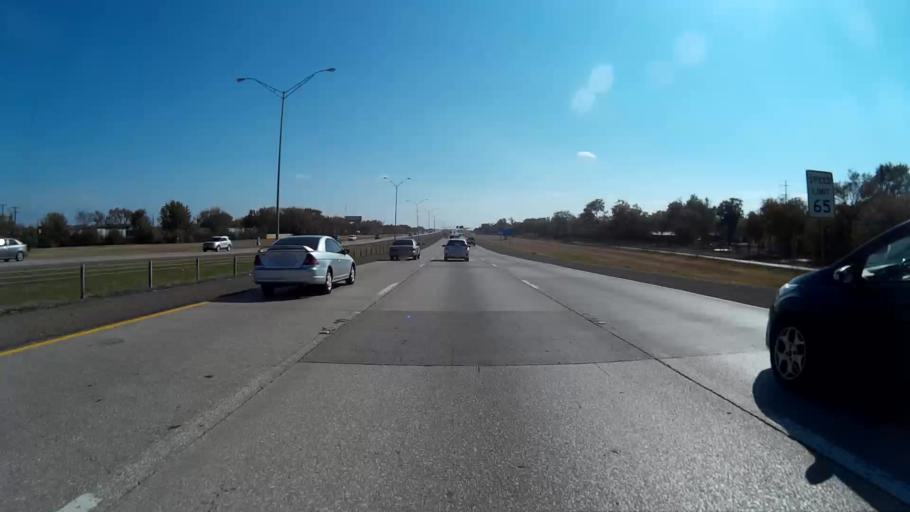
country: US
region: Texas
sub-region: Dallas County
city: Dallas
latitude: 32.7229
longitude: -96.7617
